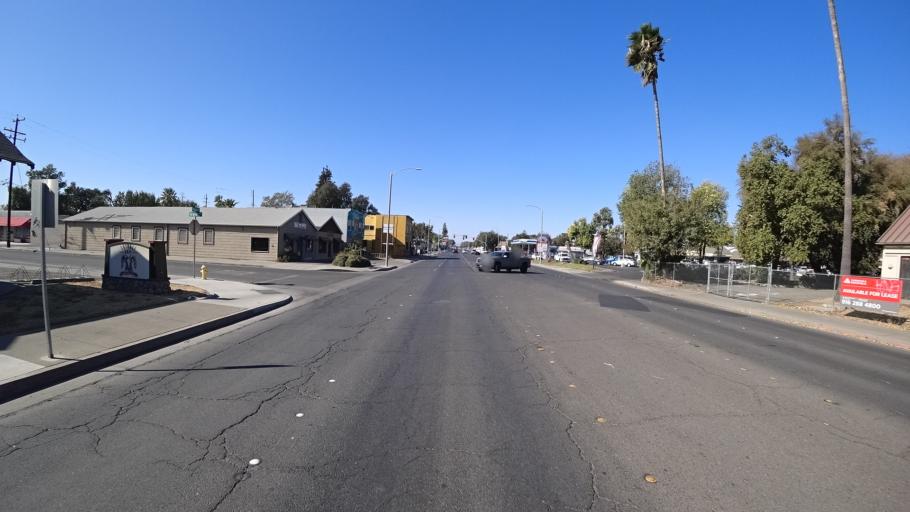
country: US
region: California
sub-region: Yolo County
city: Woodland
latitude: 38.6775
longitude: -121.7823
